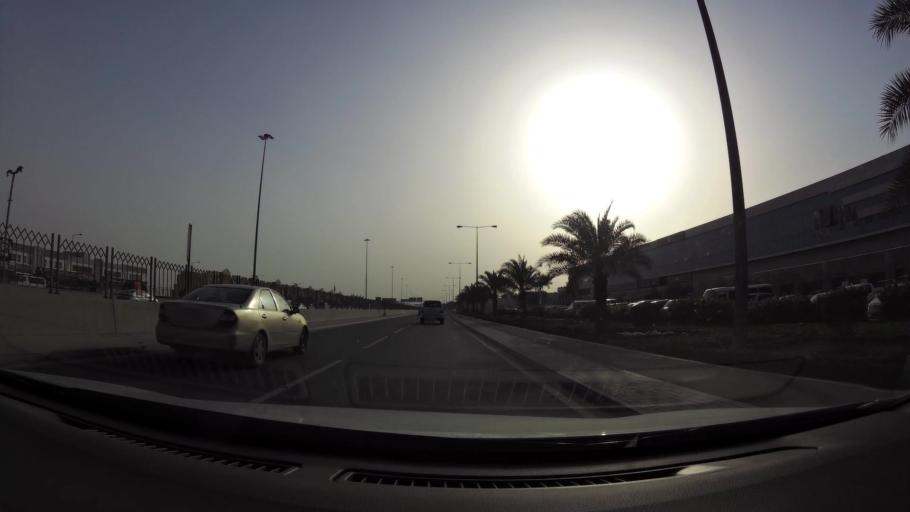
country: QA
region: Baladiyat ar Rayyan
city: Ar Rayyan
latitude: 25.2412
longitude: 51.4576
